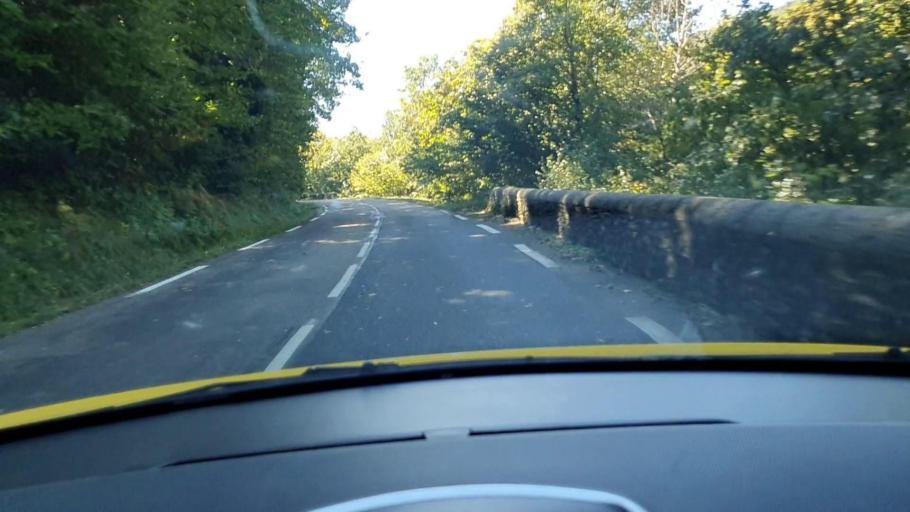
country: FR
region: Languedoc-Roussillon
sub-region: Departement du Gard
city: Le Vigan
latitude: 43.9770
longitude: 3.4162
